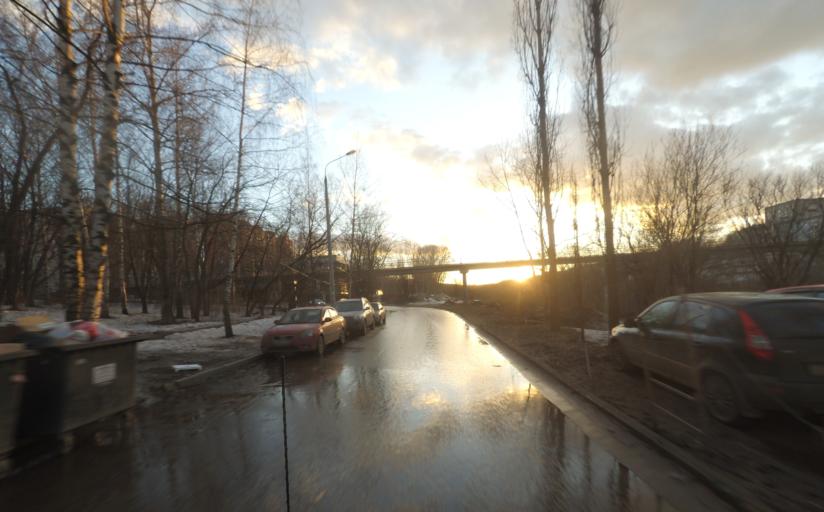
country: RU
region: Nizjnij Novgorod
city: Afonino
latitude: 56.2886
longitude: 44.0467
